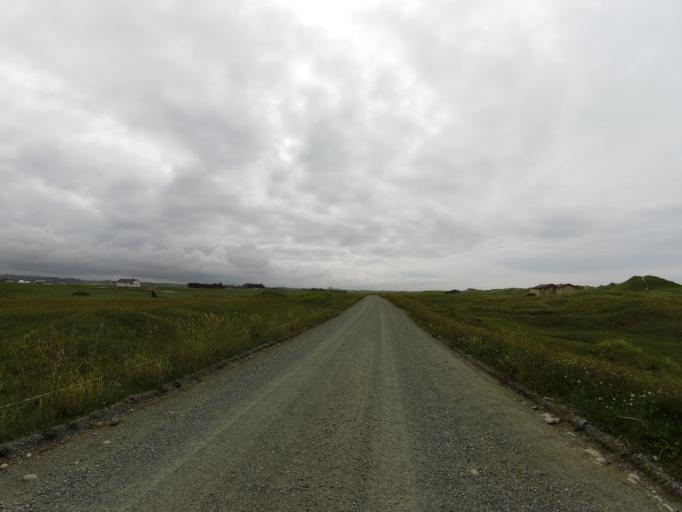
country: NO
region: Rogaland
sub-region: Klepp
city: Kleppe
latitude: 58.8085
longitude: 5.5508
